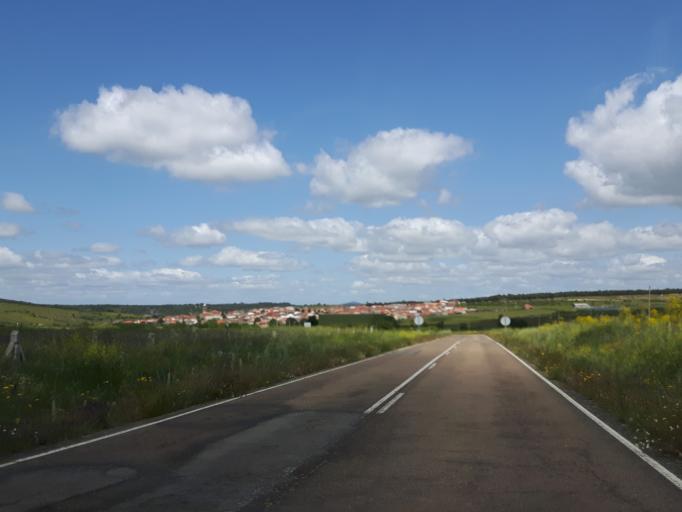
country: ES
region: Castille and Leon
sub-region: Provincia de Salamanca
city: Villar de Ciervo
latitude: 40.7329
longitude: -6.7267
